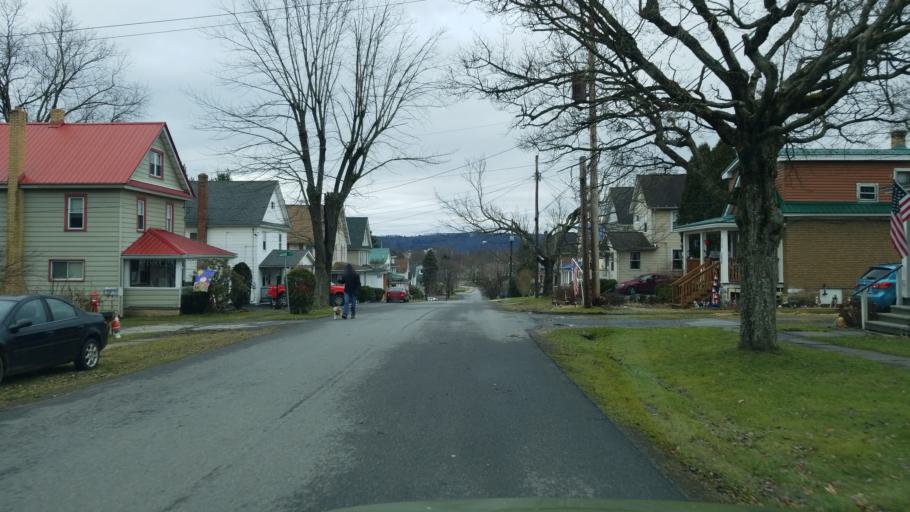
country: US
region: Pennsylvania
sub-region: Clearfield County
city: Clearfield
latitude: 41.0352
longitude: -78.4425
